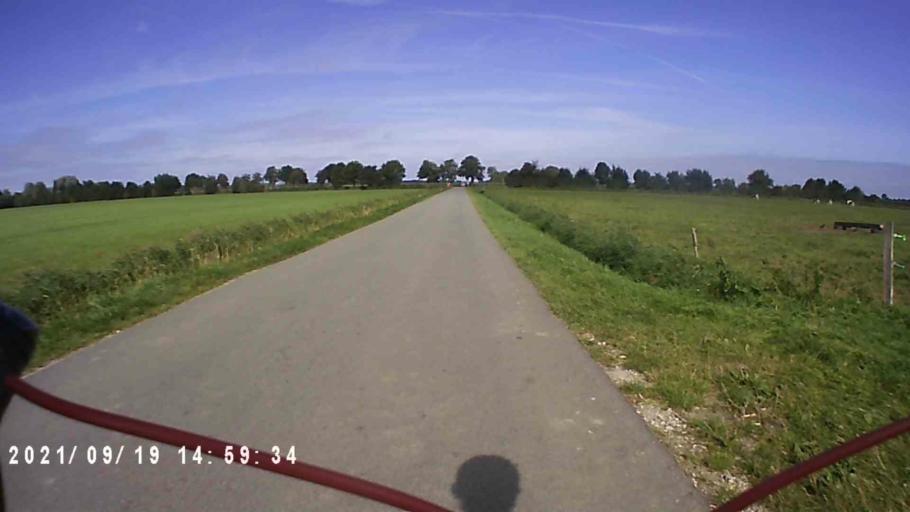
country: DE
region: Lower Saxony
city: Bunde
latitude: 53.1552
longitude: 7.2092
